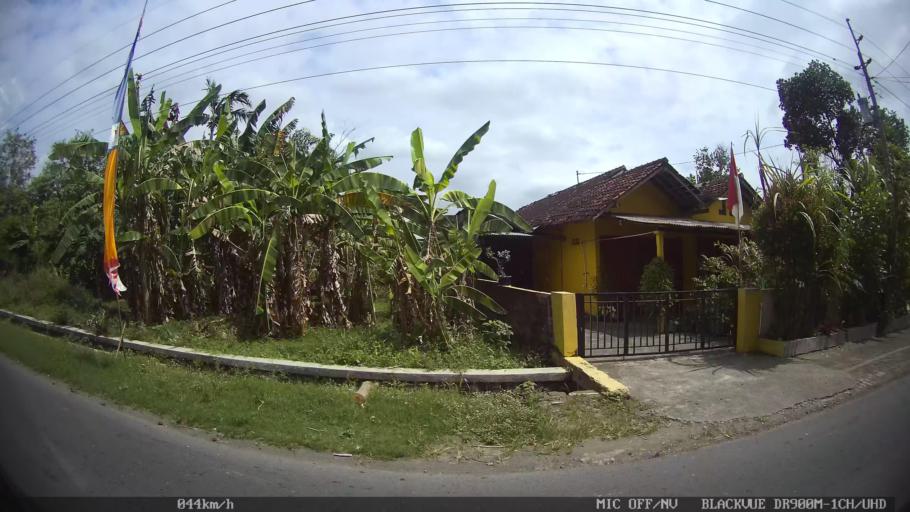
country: ID
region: Daerah Istimewa Yogyakarta
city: Depok
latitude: -7.8028
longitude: 110.4533
